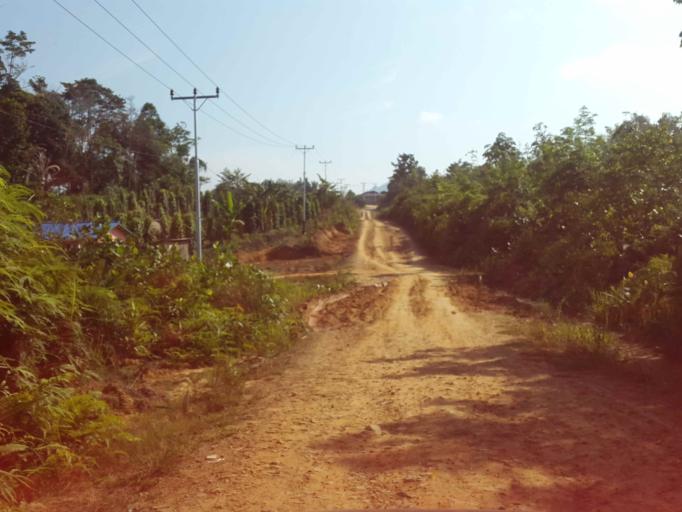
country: MY
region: Sarawak
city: Simanggang
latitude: 0.9335
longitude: 111.0900
